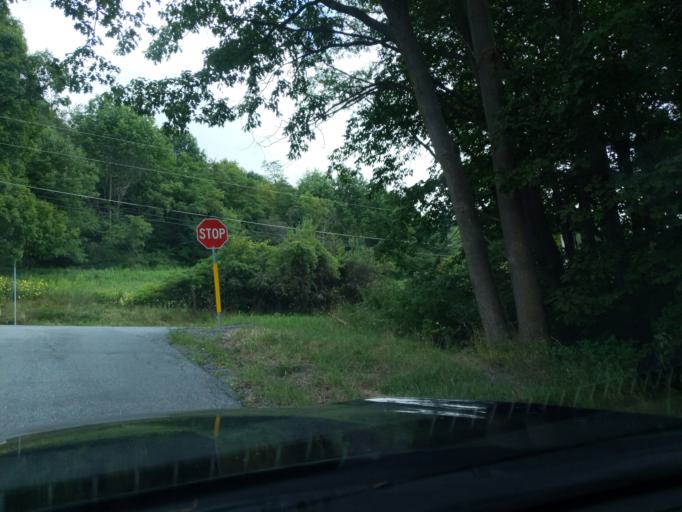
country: US
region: Pennsylvania
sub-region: Cambria County
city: Portage
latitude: 40.3520
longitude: -78.5867
